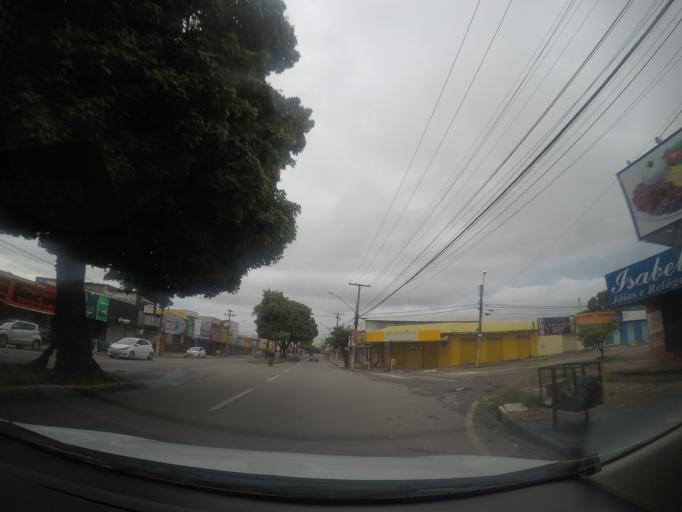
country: BR
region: Goias
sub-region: Goiania
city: Goiania
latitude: -16.7212
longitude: -49.3213
